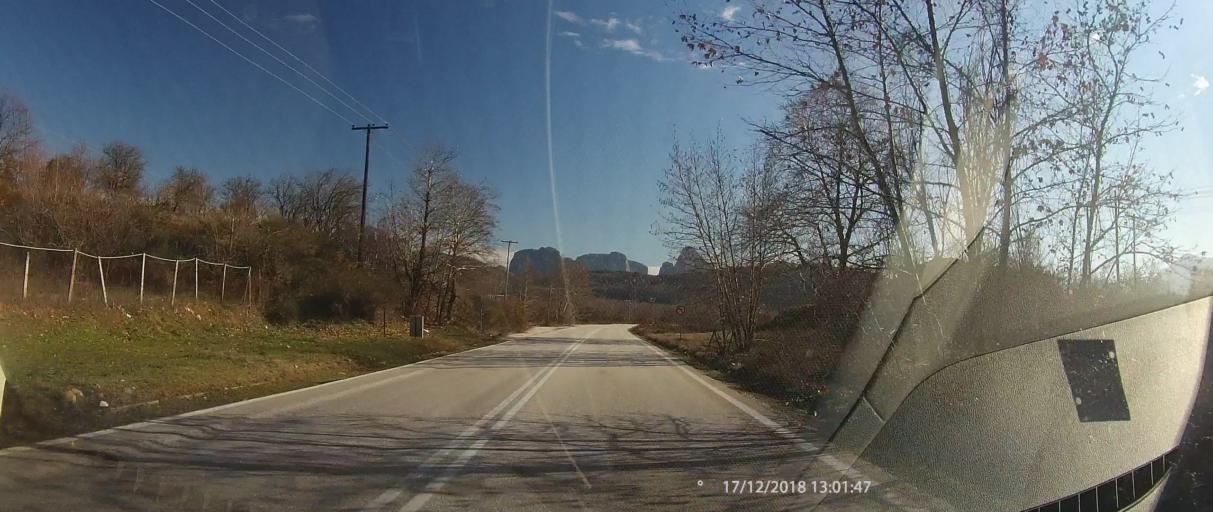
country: GR
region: Thessaly
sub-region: Trikala
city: Kastraki
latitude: 39.7304
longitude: 21.5887
